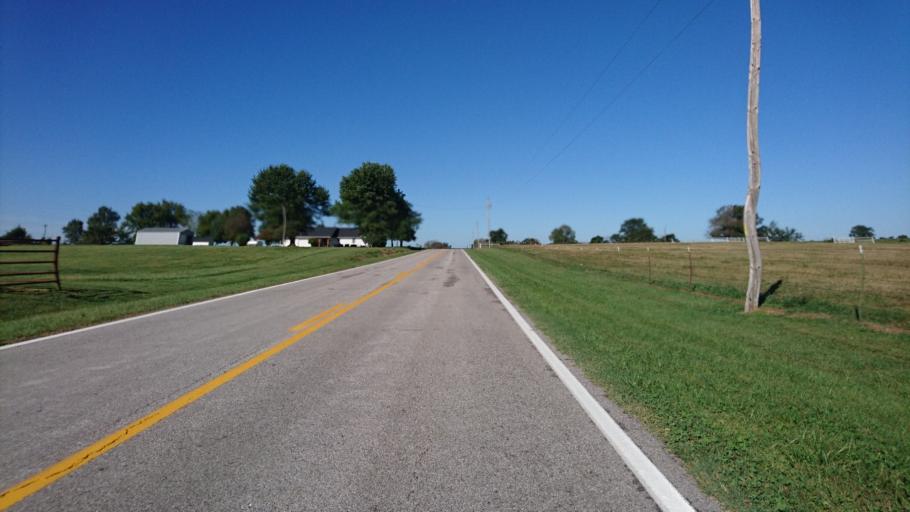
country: US
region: Missouri
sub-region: Greene County
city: Ash Grove
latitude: 37.1940
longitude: -93.6640
